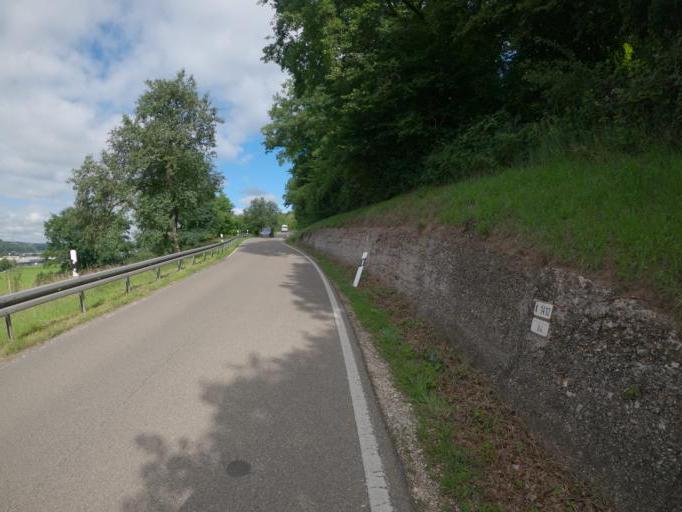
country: DE
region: Baden-Wuerttemberg
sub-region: Regierungsbezirk Stuttgart
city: Albershausen
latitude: 48.7220
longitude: 9.5565
